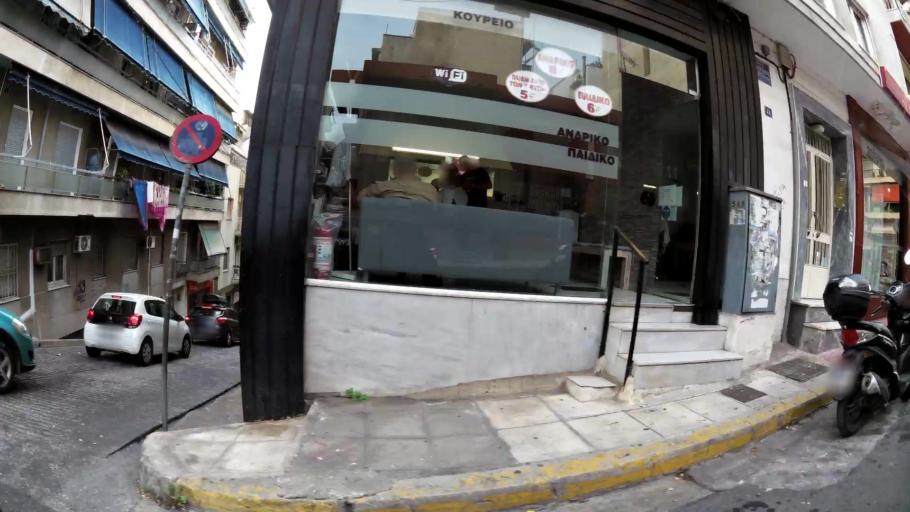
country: GR
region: Attica
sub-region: Nomarchia Athinas
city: Kipseli
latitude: 37.9944
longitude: 23.7505
